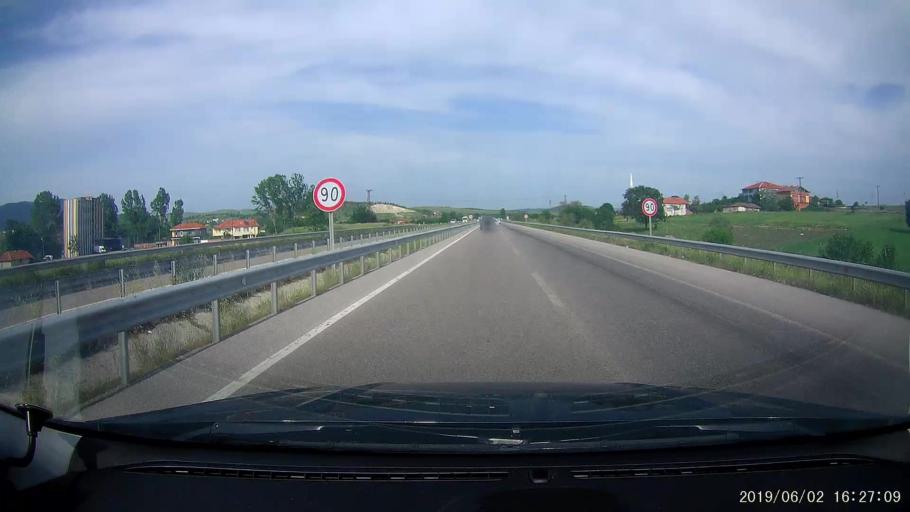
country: TR
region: Samsun
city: Ladik
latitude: 41.0016
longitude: 35.8207
